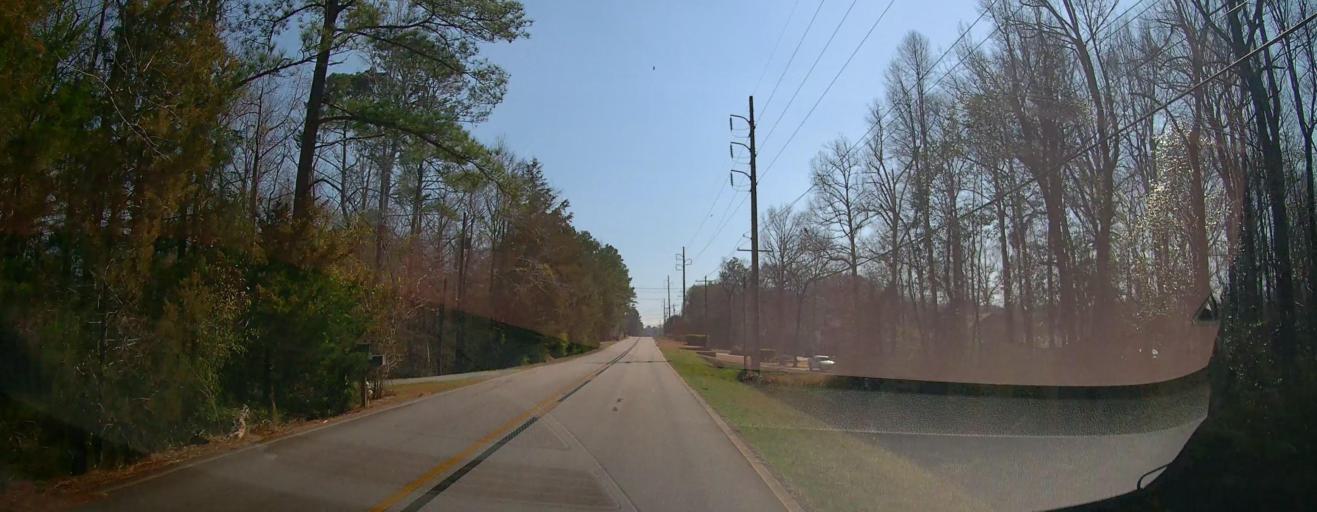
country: US
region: Georgia
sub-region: Houston County
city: Perry
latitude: 32.4700
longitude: -83.7589
